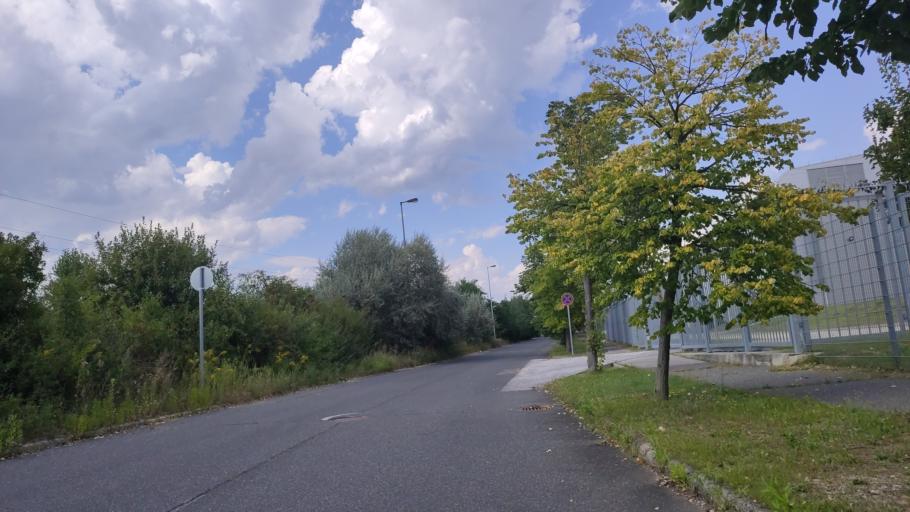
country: HU
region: Pest
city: Toeroekbalint
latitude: 47.4419
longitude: 18.8825
